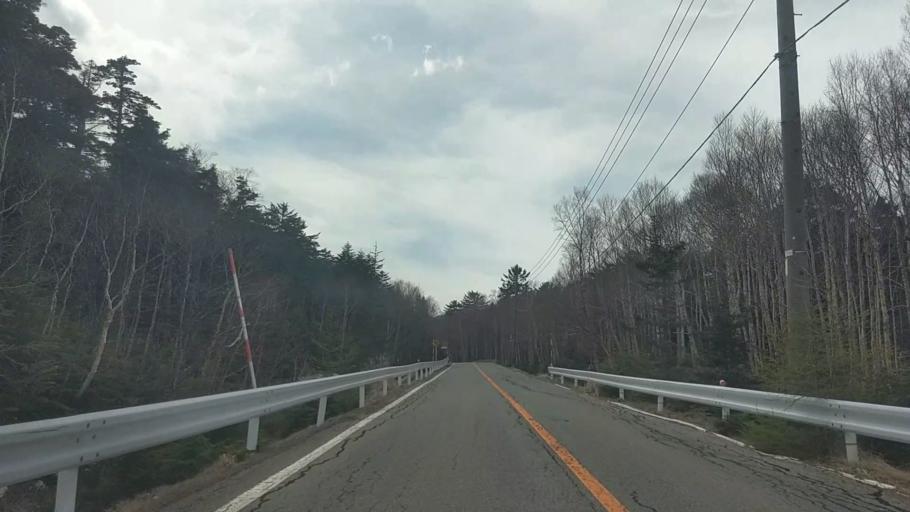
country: JP
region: Nagano
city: Saku
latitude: 36.0575
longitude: 138.3579
